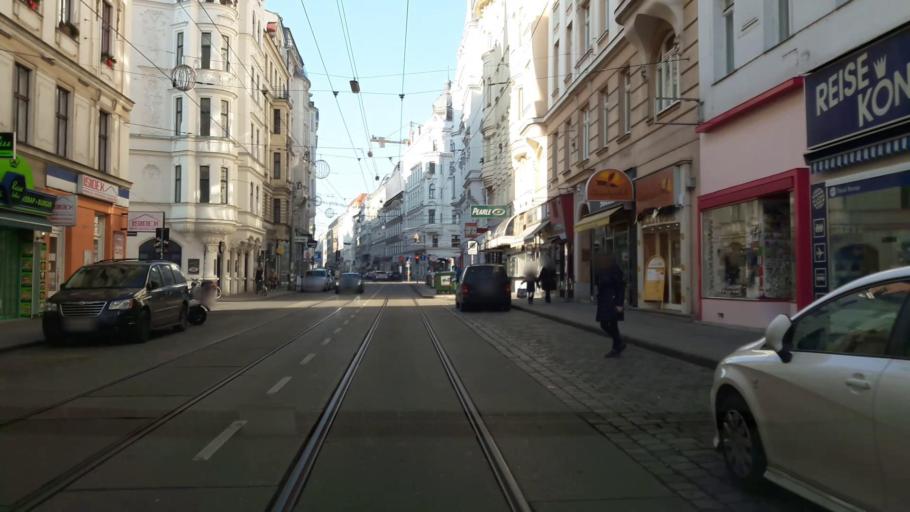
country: AT
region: Vienna
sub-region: Wien Stadt
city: Vienna
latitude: 48.2103
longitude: 16.3454
